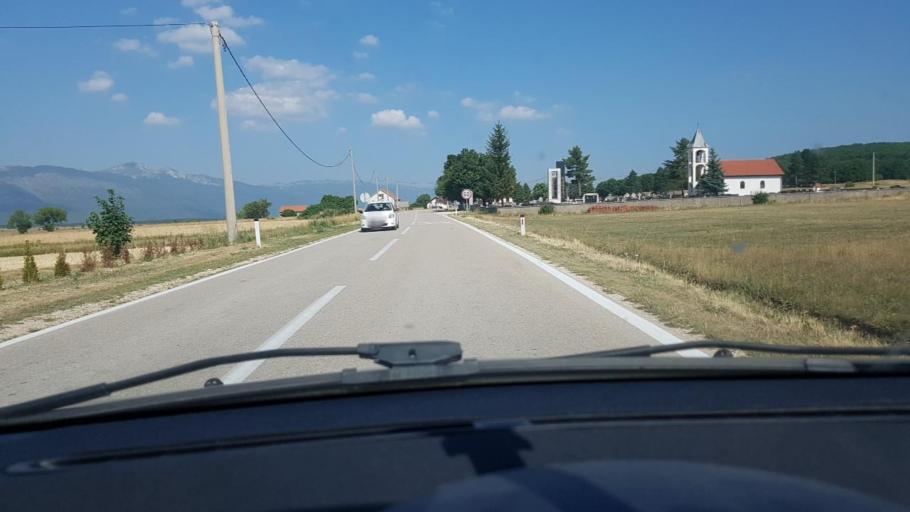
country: BA
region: Federation of Bosnia and Herzegovina
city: Glamoc
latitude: 43.9213
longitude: 16.7837
